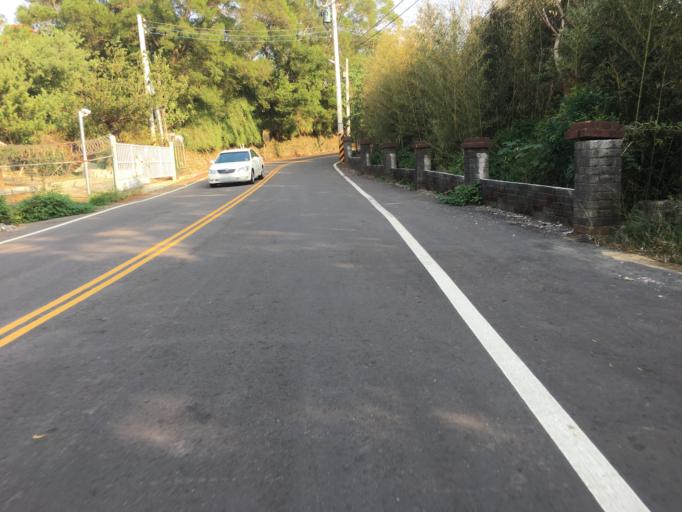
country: TW
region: Taiwan
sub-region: Hsinchu
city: Hsinchu
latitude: 24.7481
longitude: 121.0349
